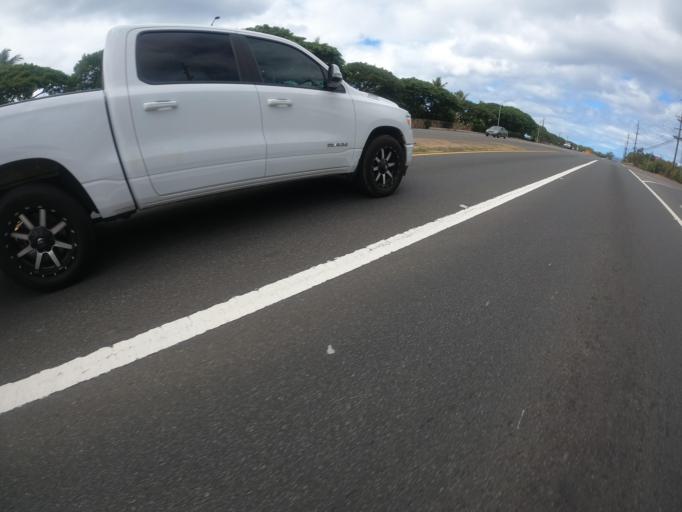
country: US
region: Hawaii
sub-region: Honolulu County
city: Makakilo
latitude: 21.3471
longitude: -158.1252
